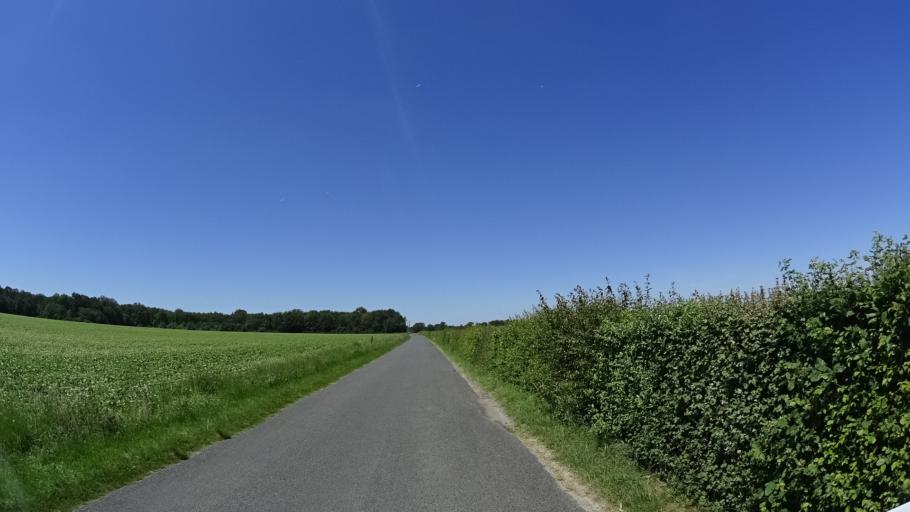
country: FR
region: Pays de la Loire
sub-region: Departement de Maine-et-Loire
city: Chenehutte-Treves-Cunault
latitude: 47.2860
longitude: -0.1414
